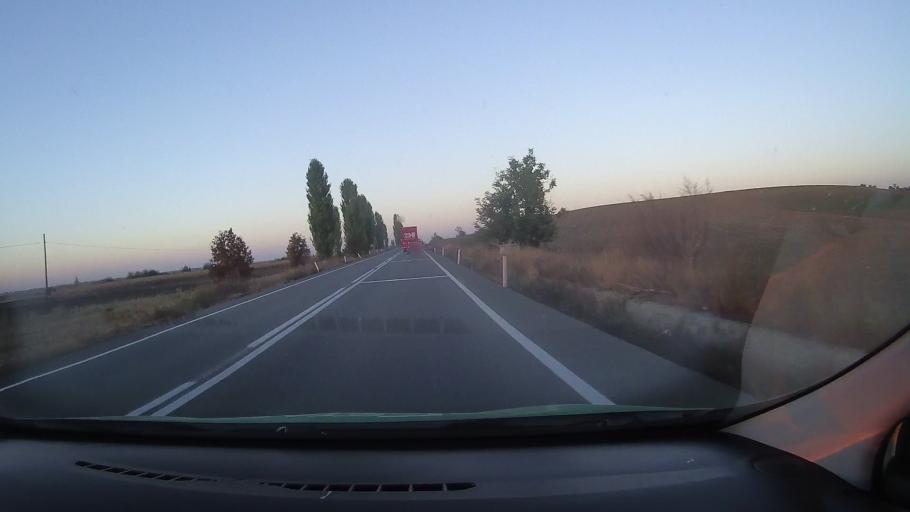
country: RO
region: Bihor
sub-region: Comuna Cherechiu
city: Cherechiu
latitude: 47.3895
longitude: 22.1464
